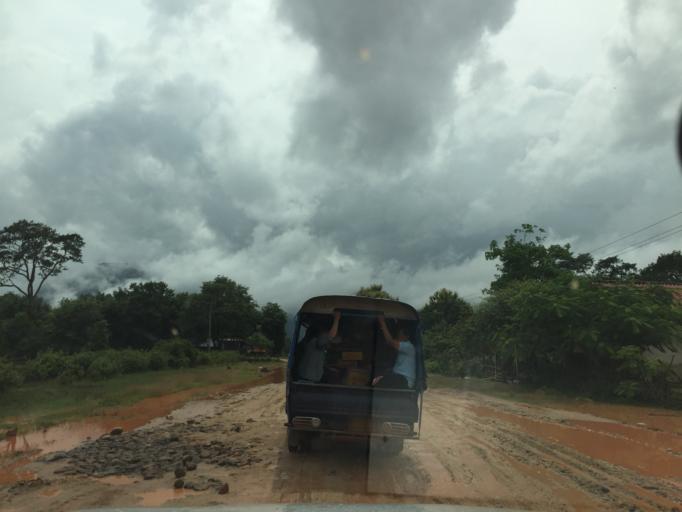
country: LA
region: Attapu
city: Attapu
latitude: 14.8076
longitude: 106.7694
